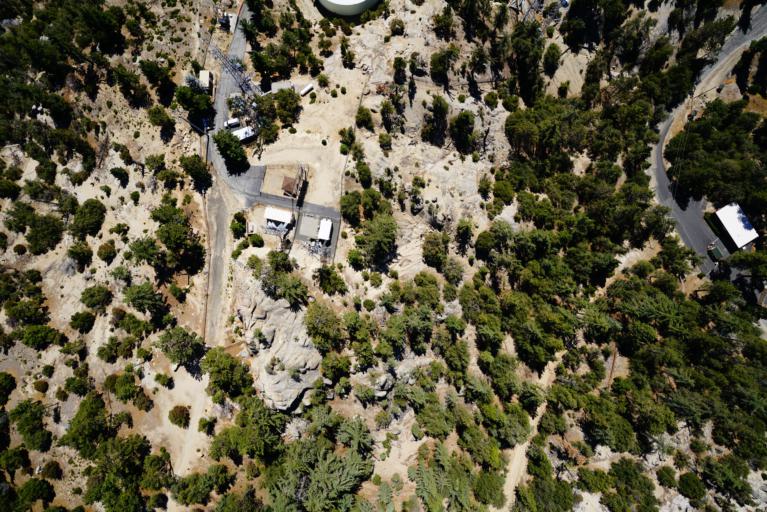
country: US
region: California
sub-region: Riverside County
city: Idyllwild-Pine Cove
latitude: 33.7660
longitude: -116.7318
